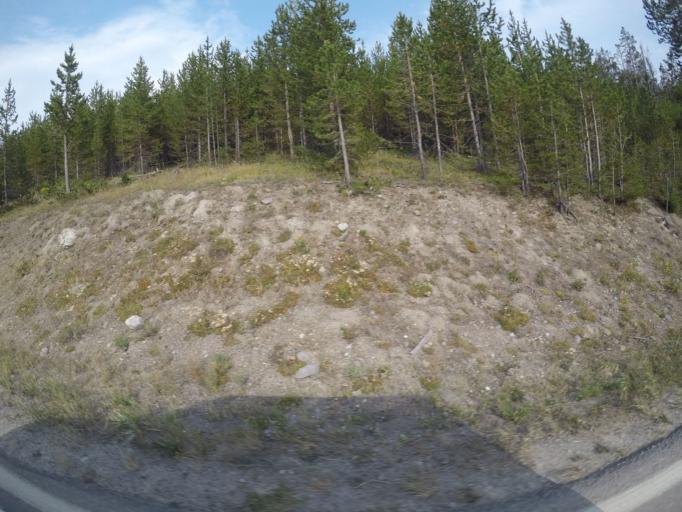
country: US
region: Montana
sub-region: Gallatin County
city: West Yellowstone
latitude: 44.8695
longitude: -110.7381
